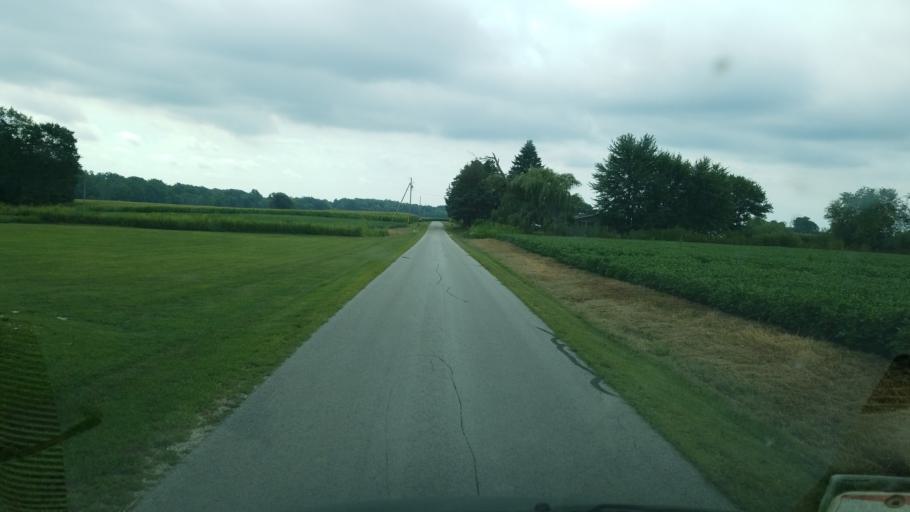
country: US
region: Ohio
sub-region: Sandusky County
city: Green Springs
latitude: 41.2193
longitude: -83.1357
